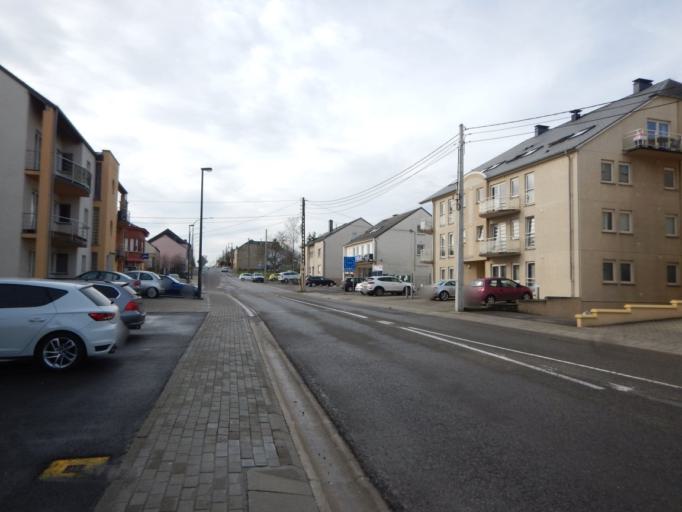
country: BE
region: Wallonia
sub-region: Province du Luxembourg
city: Aubange
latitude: 49.5612
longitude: 5.7952
